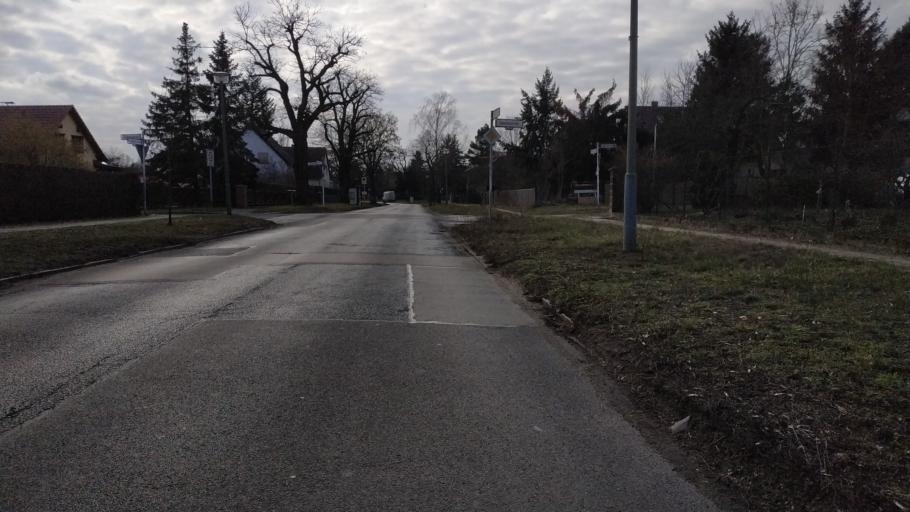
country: DE
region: Berlin
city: Hellersdorf
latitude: 52.5221
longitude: 13.6061
